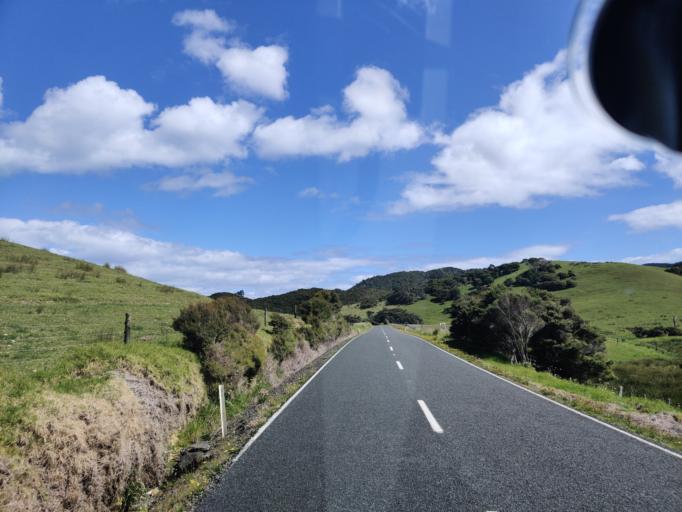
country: NZ
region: Northland
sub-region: Far North District
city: Paihia
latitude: -35.2720
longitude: 174.2796
